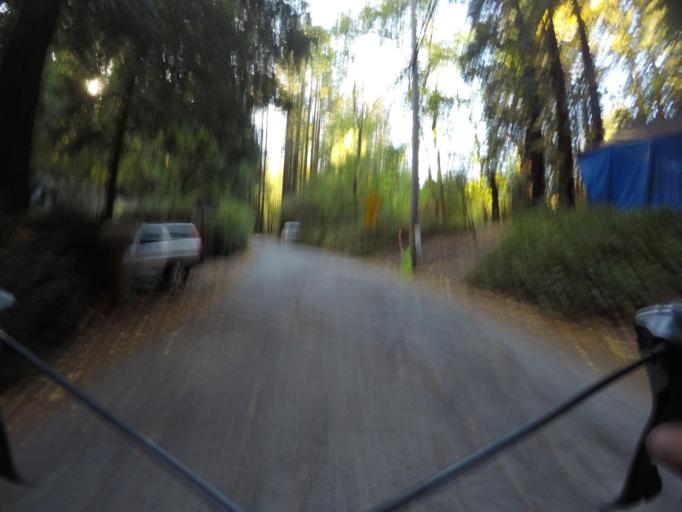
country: US
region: California
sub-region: Santa Cruz County
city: Boulder Creek
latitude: 37.1215
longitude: -122.1186
